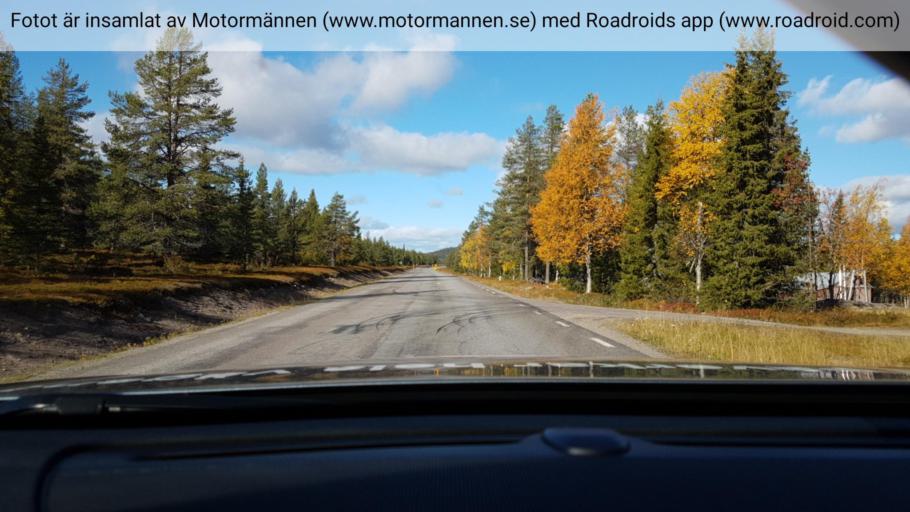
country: SE
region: Norrbotten
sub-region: Arjeplogs Kommun
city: Arjeplog
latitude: 65.9090
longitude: 18.3485
